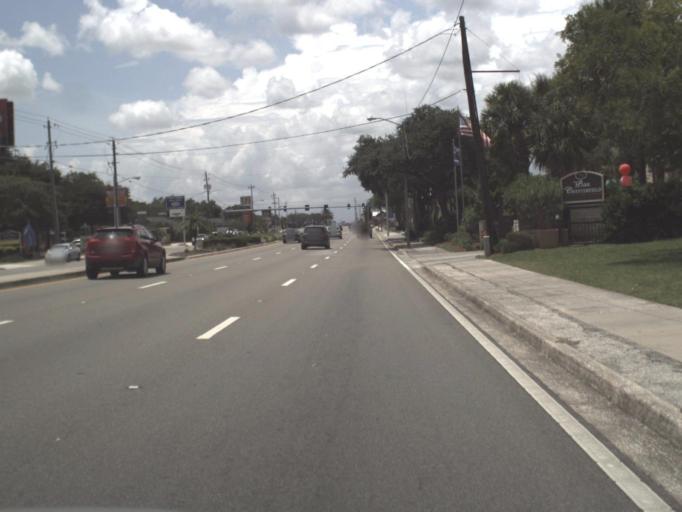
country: US
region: Florida
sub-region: Hillsborough County
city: Temple Terrace
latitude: 28.0327
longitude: -82.3992
